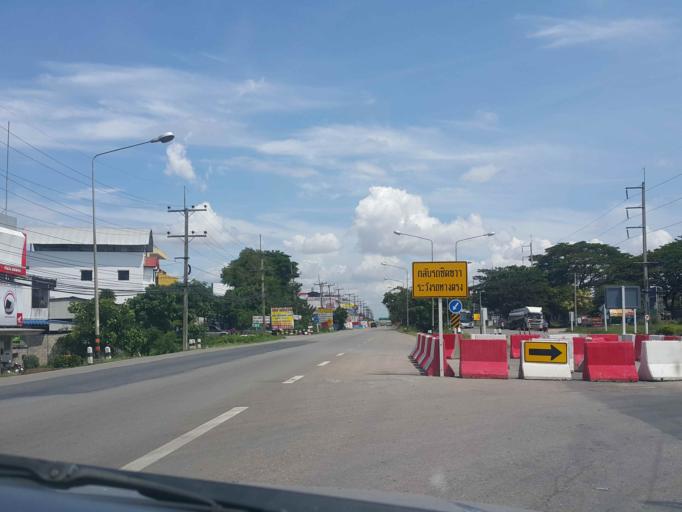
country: TH
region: Phayao
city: Phayao
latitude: 19.1637
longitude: 99.9125
